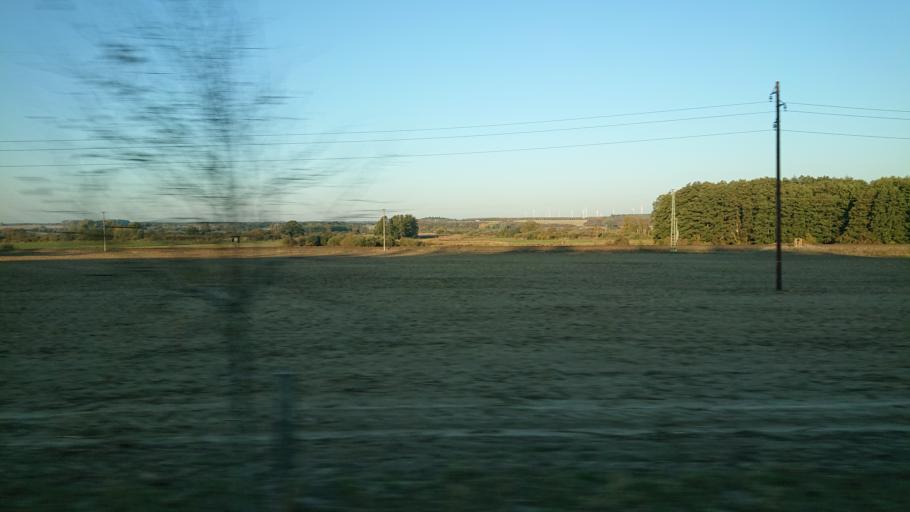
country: DE
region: Mecklenburg-Vorpommern
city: Trollenhagen
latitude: 53.6261
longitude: 13.2624
